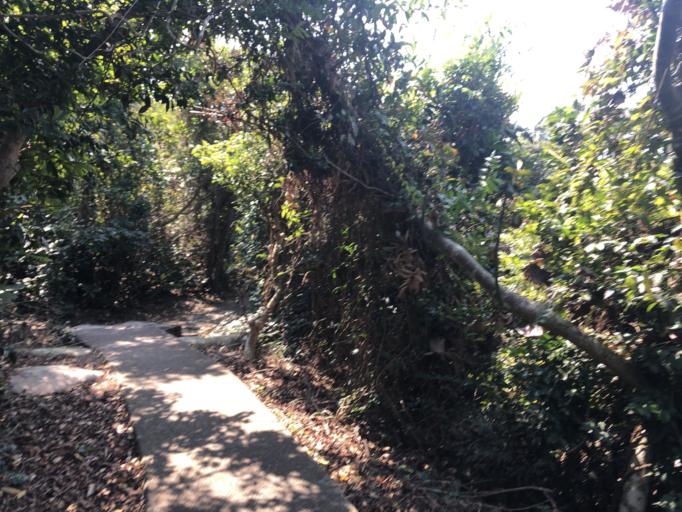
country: HK
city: Sok Kwu Wan
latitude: 22.1654
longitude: 114.2584
